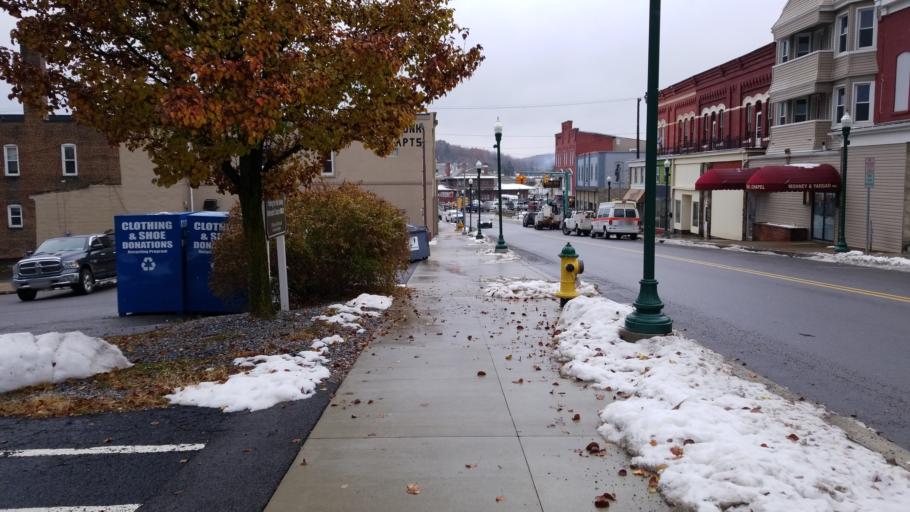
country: US
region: Pennsylvania
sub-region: Clearfield County
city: DuBois
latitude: 41.1201
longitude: -78.7640
